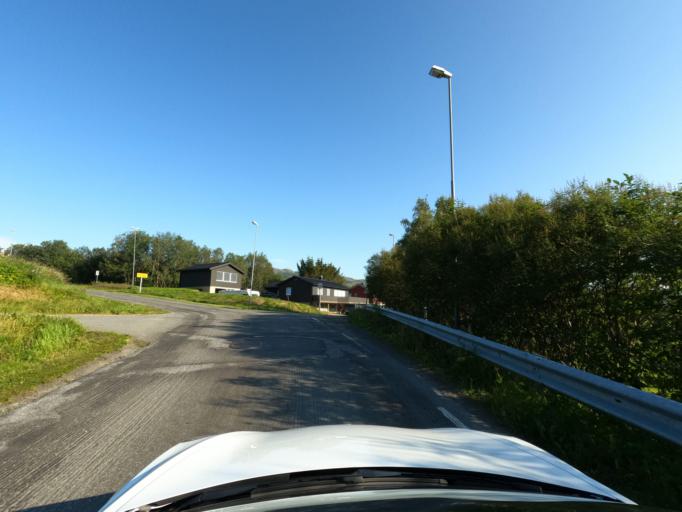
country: NO
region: Nordland
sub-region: Narvik
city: Bjerkvik
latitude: 68.5523
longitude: 17.5612
